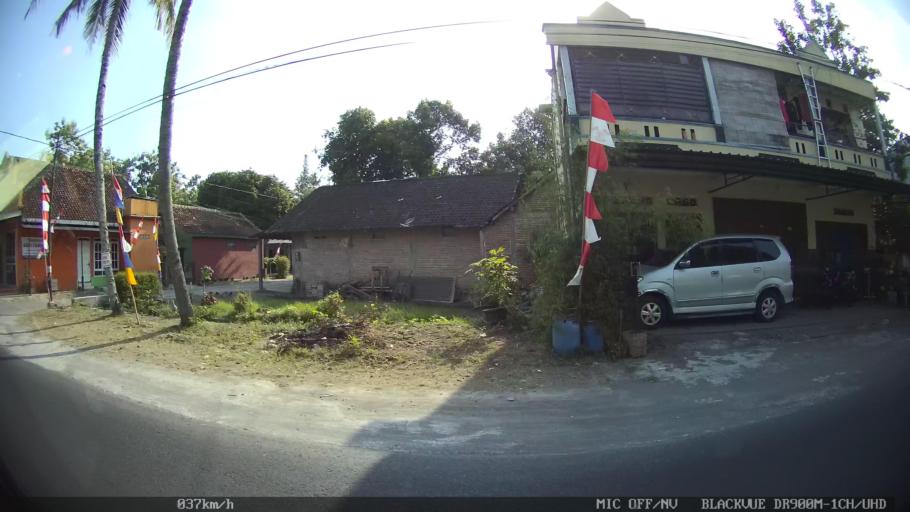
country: ID
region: Daerah Istimewa Yogyakarta
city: Bantul
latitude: -7.8891
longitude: 110.3035
